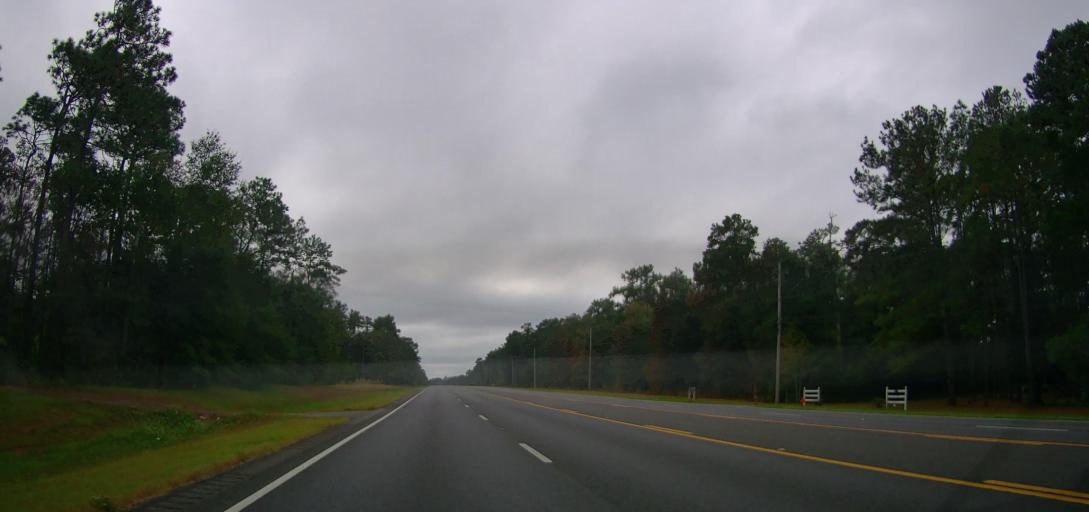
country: US
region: Georgia
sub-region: Thomas County
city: Thomasville
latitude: 30.9062
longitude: -83.9245
